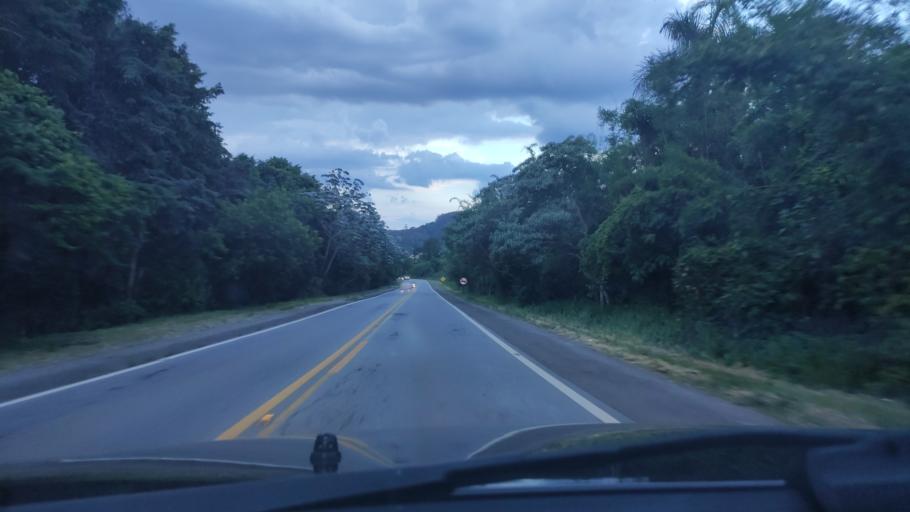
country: BR
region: Sao Paulo
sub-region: Braganca Paulista
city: Braganca Paulista
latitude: -22.8781
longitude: -46.5353
